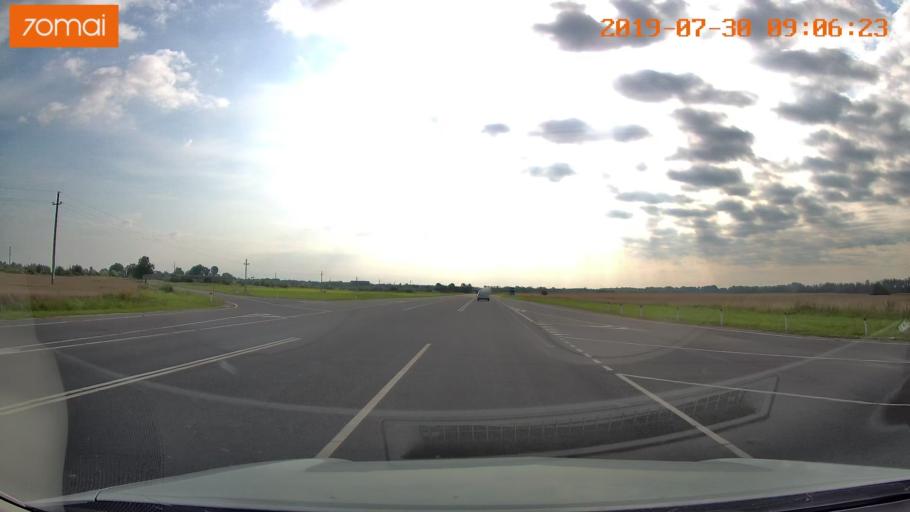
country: RU
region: Kaliningrad
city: Gusev
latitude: 54.6094
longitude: 22.3345
